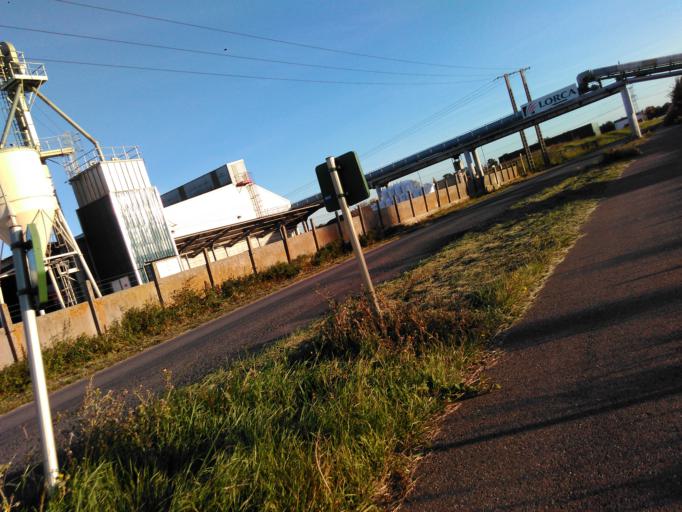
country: FR
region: Lorraine
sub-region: Departement de la Moselle
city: Maizieres-les-Metz
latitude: 49.2060
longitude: 6.1814
